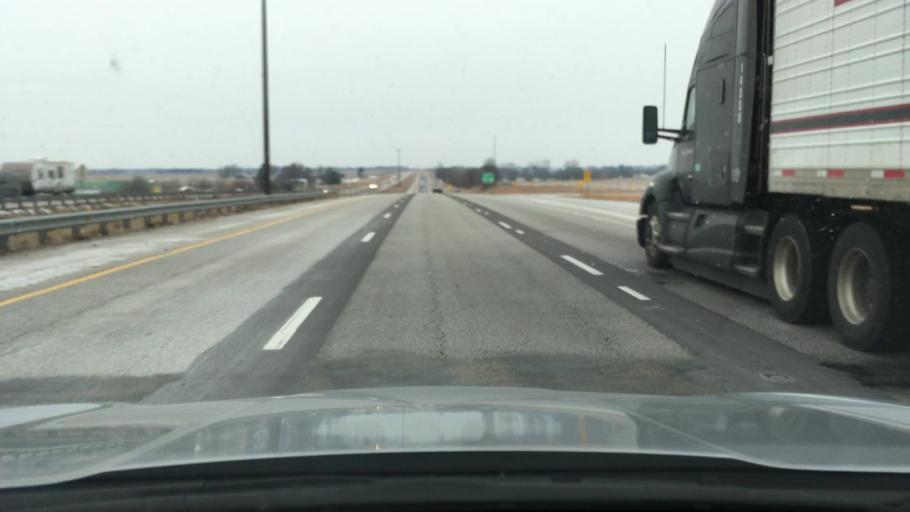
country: US
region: Illinois
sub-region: Sangamon County
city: Divernon
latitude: 39.5904
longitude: -89.6464
